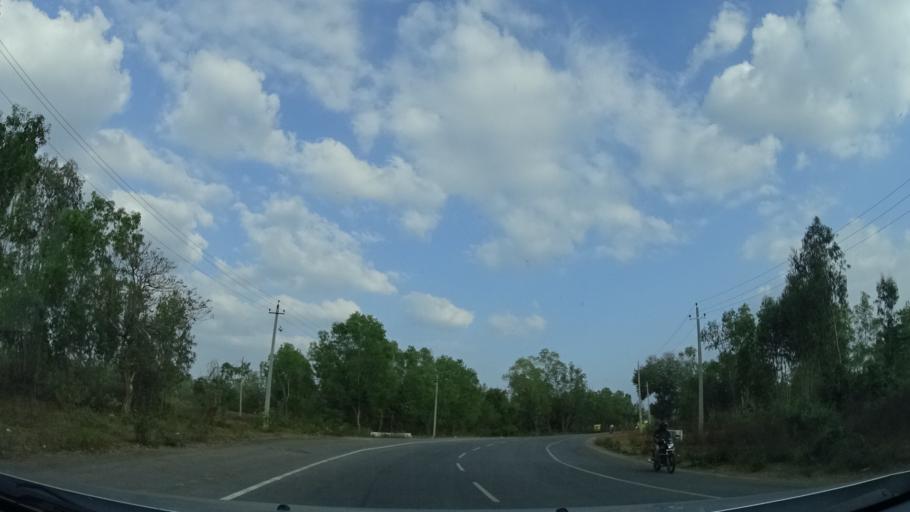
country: IN
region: Karnataka
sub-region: Mandya
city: Malavalli
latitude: 12.3630
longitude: 76.9780
